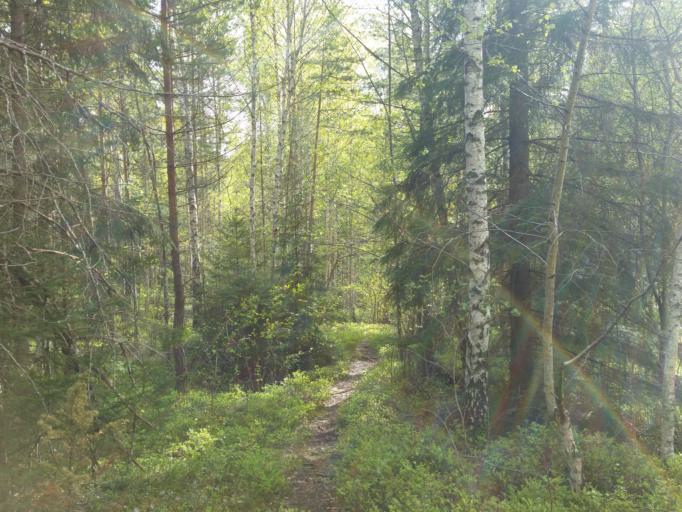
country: SE
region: Stockholm
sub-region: Sollentuna Kommun
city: Sollentuna
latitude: 59.4693
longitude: 17.9413
